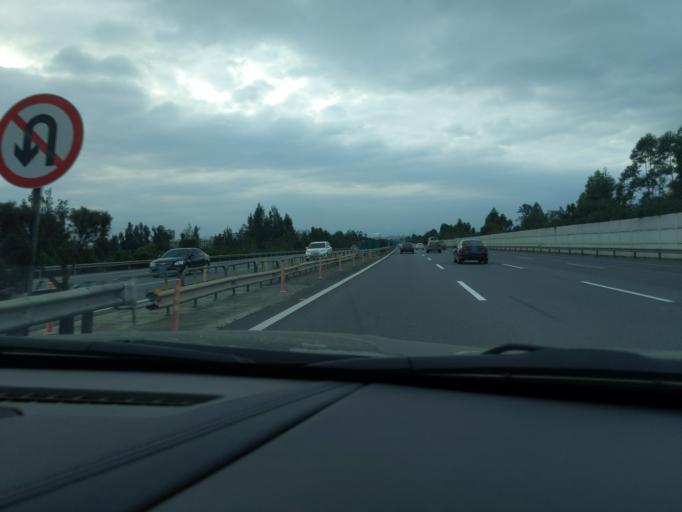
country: CN
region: Fujian
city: Maxiang
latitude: 24.6811
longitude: 118.2832
